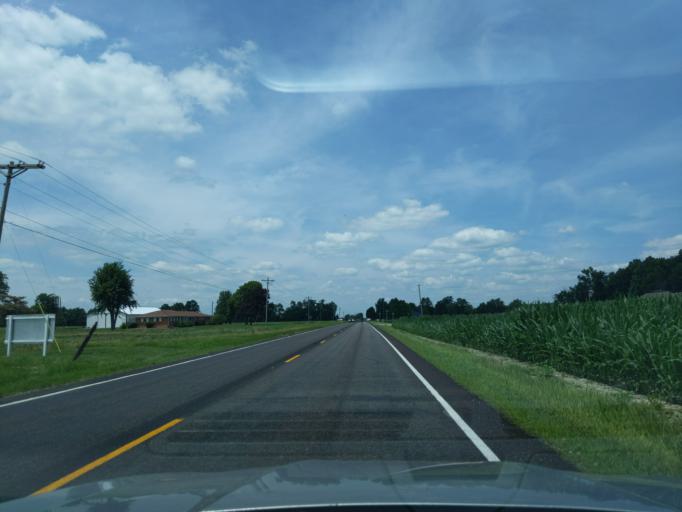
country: US
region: Indiana
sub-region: Ripley County
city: Osgood
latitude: 39.2175
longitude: -85.3337
